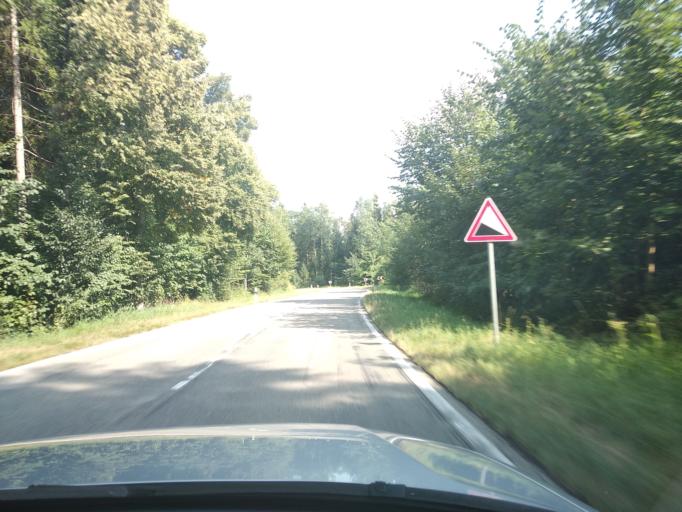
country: DE
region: Baden-Wuerttemberg
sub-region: Tuebingen Region
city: Leutkirch im Allgau
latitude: 47.8691
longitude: 10.0024
